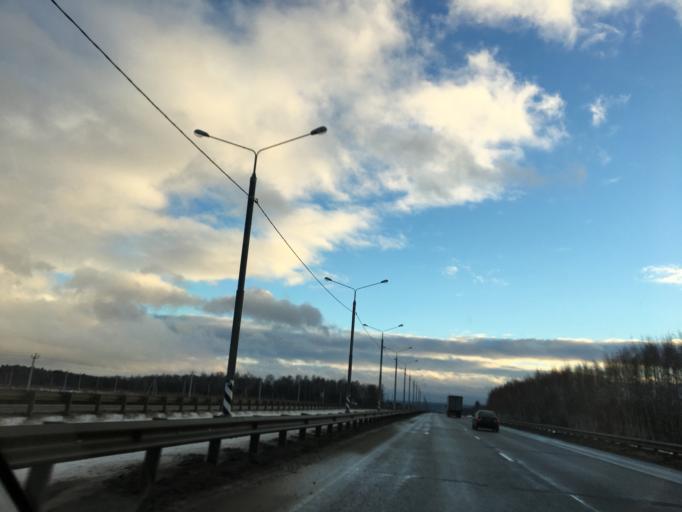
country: RU
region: Tula
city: Zaokskiy
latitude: 54.7984
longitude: 37.4852
